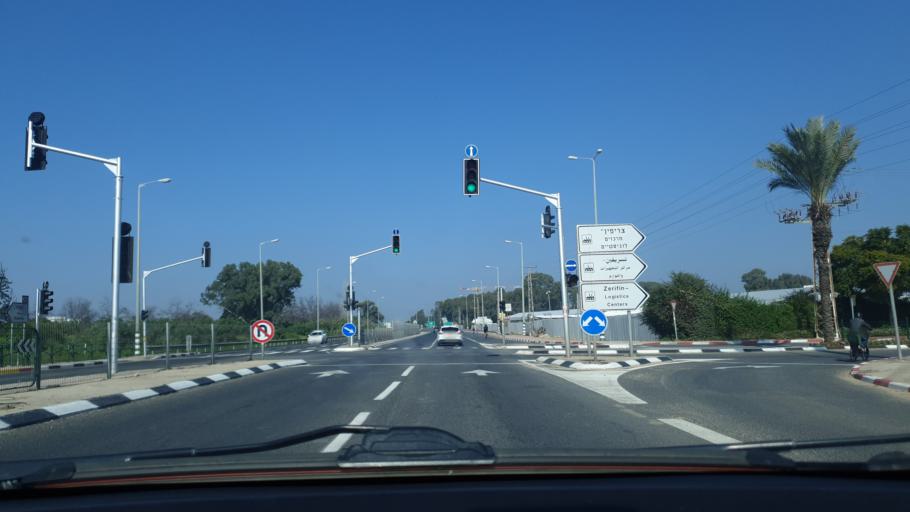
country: IL
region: Central District
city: Kefar Habad
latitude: 31.9634
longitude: 34.8489
